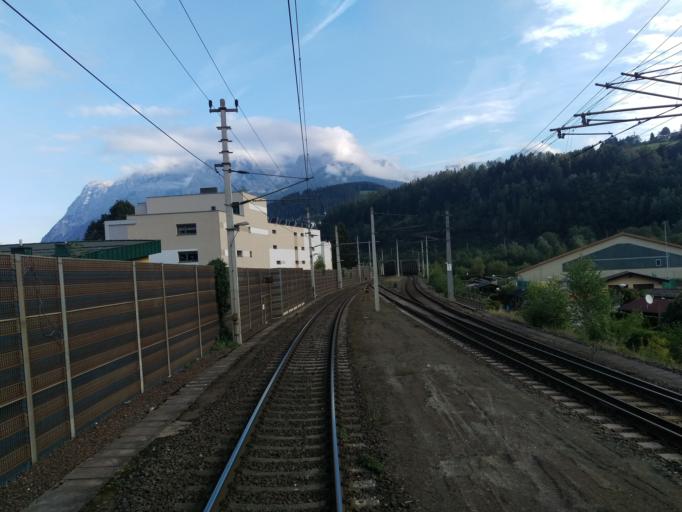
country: AT
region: Salzburg
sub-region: Politischer Bezirk Sankt Johann im Pongau
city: Bischofshofen
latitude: 47.4238
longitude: 13.2197
